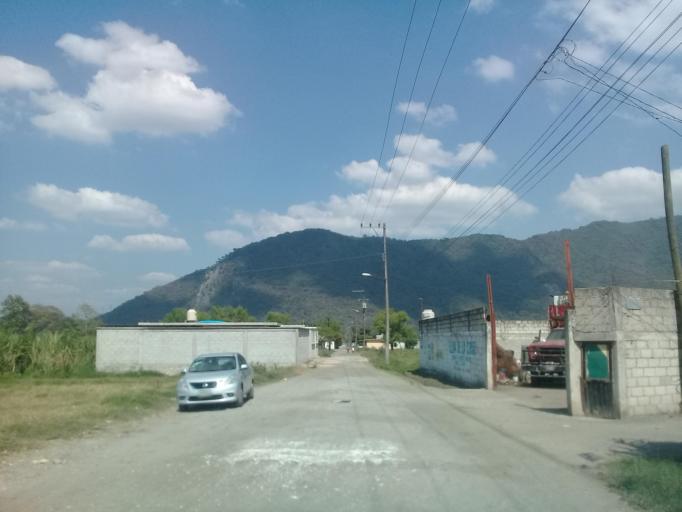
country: MX
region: Veracruz
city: Jalapilla
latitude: 18.8240
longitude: -97.0817
